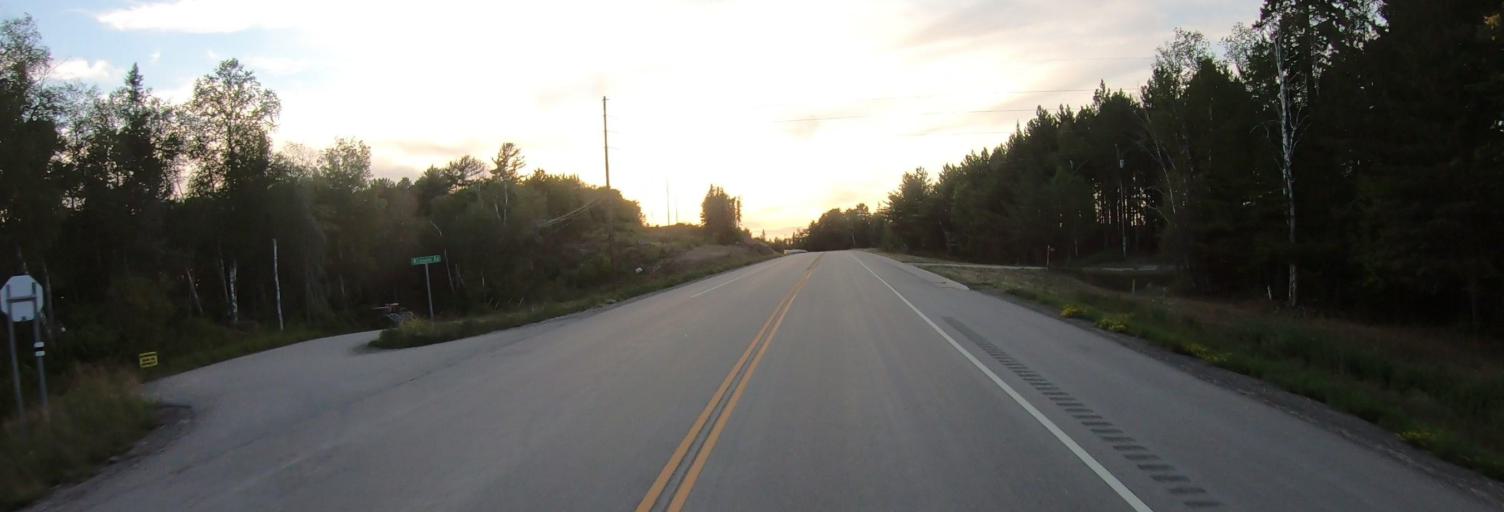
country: US
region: Minnesota
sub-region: Saint Louis County
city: Babbitt
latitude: 47.8550
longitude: -92.0631
